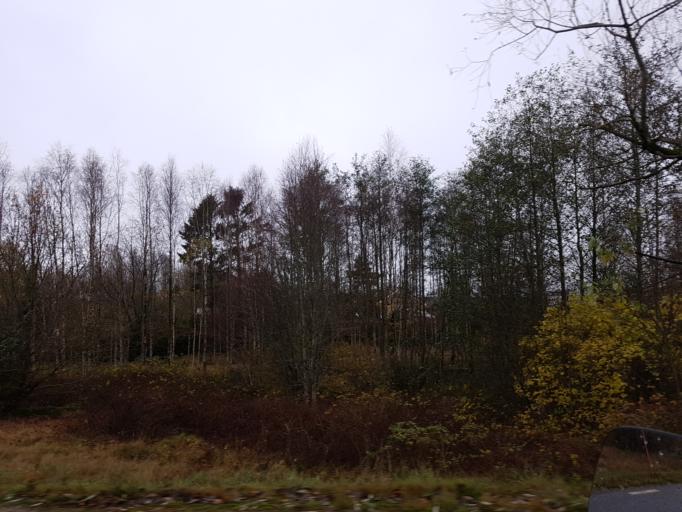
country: SE
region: Vaestra Goetaland
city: Svanesund
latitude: 58.1653
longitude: 11.7884
